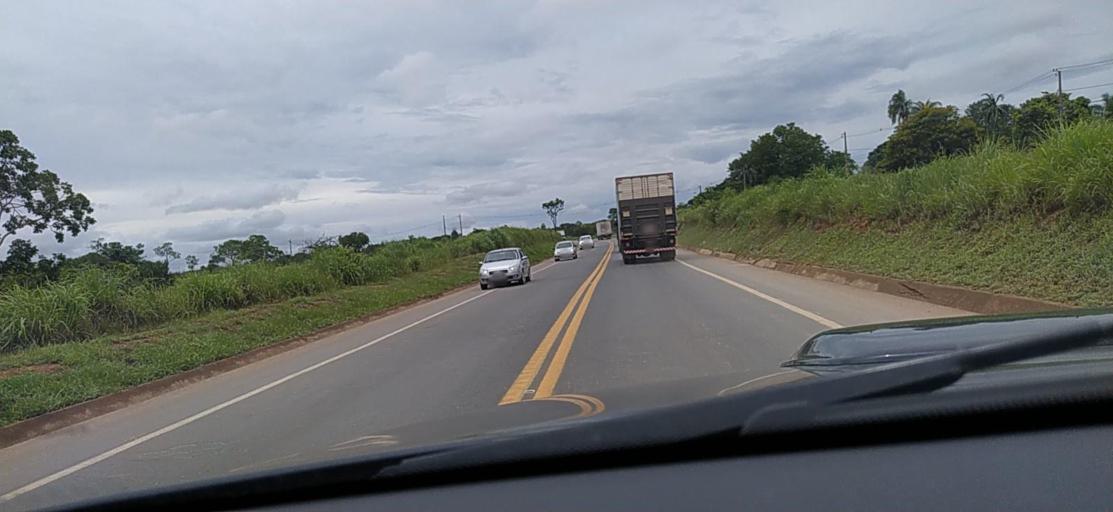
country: BR
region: Minas Gerais
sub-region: Curvelo
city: Curvelo
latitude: -18.7253
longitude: -44.4420
